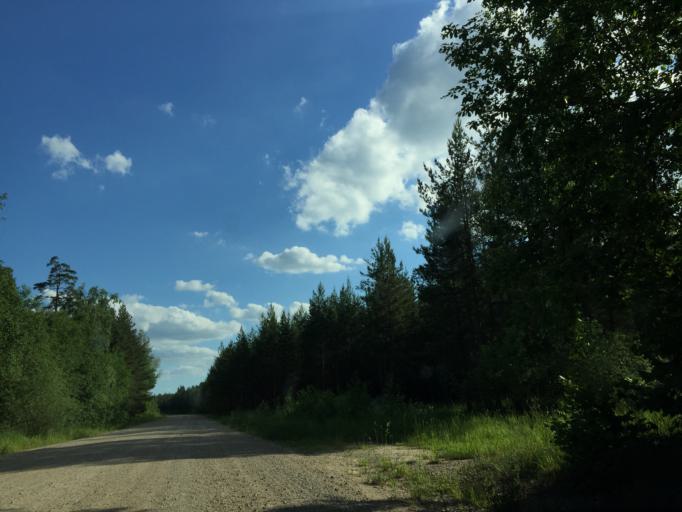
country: LV
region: Kandava
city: Kandava
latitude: 56.8586
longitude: 22.7529
